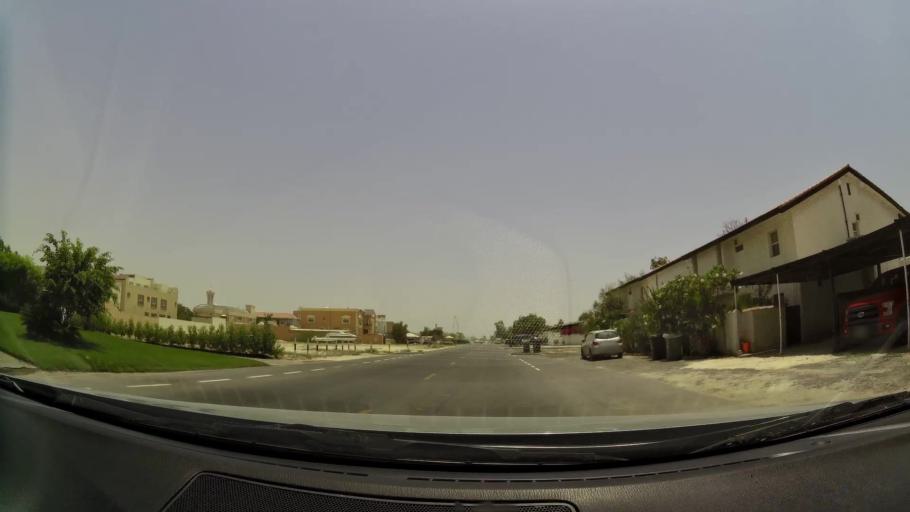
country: AE
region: Dubai
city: Dubai
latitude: 25.1703
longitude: 55.2203
